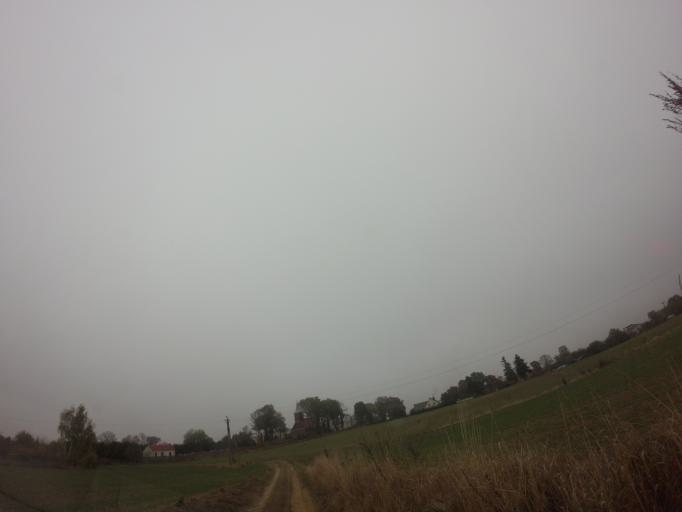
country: PL
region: West Pomeranian Voivodeship
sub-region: Powiat choszczenski
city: Pelczyce
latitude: 53.0206
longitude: 15.3646
